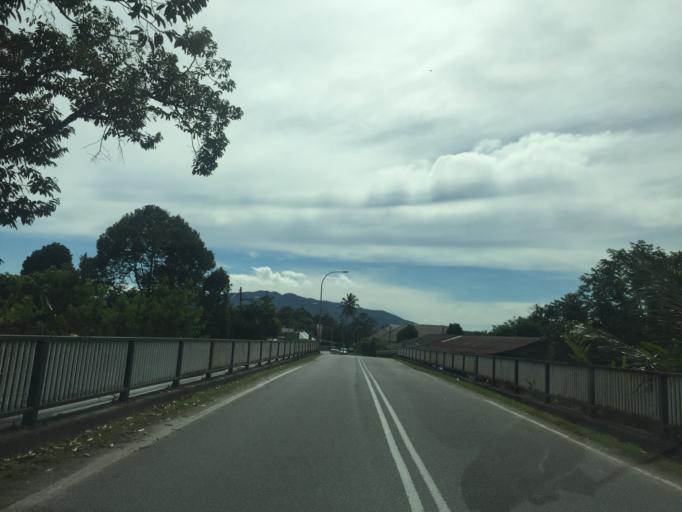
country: MY
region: Negeri Sembilan
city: Seremban
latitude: 2.7302
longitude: 101.9627
